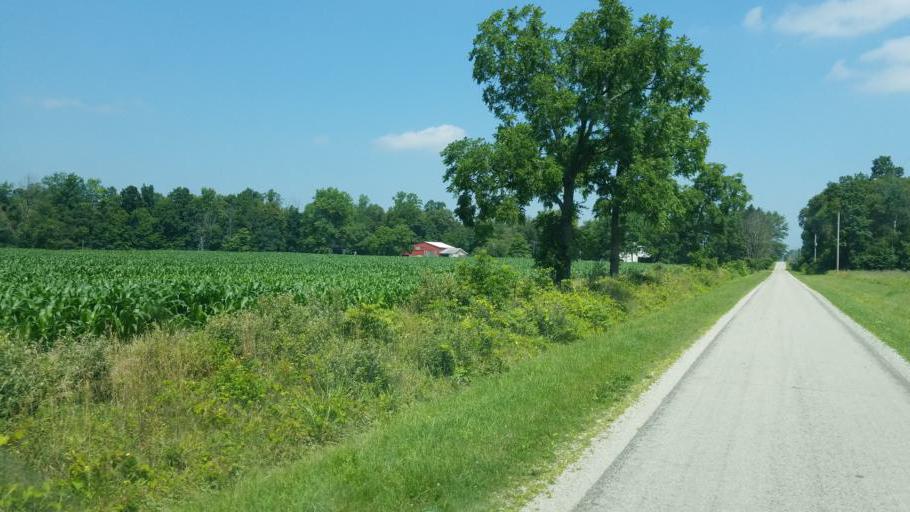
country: US
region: Ohio
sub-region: Seneca County
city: Tiffin
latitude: 41.0418
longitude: -82.9771
